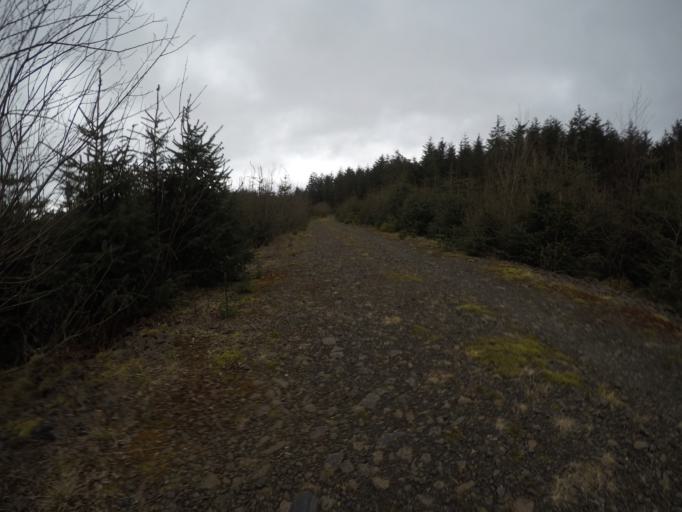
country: GB
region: Scotland
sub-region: East Ayrshire
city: Newmilns
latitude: 55.6779
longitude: -4.3569
